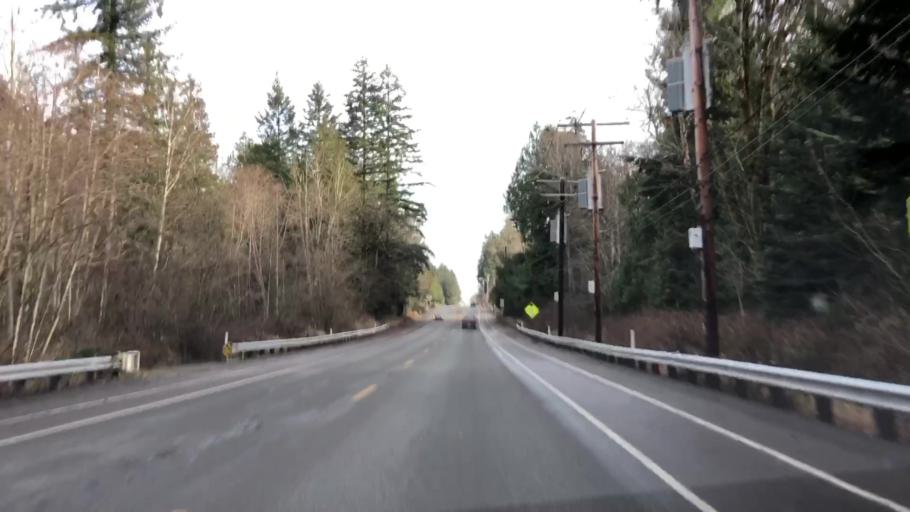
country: US
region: Washington
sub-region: Kitsap County
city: Kingston
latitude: 47.7949
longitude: -122.5300
